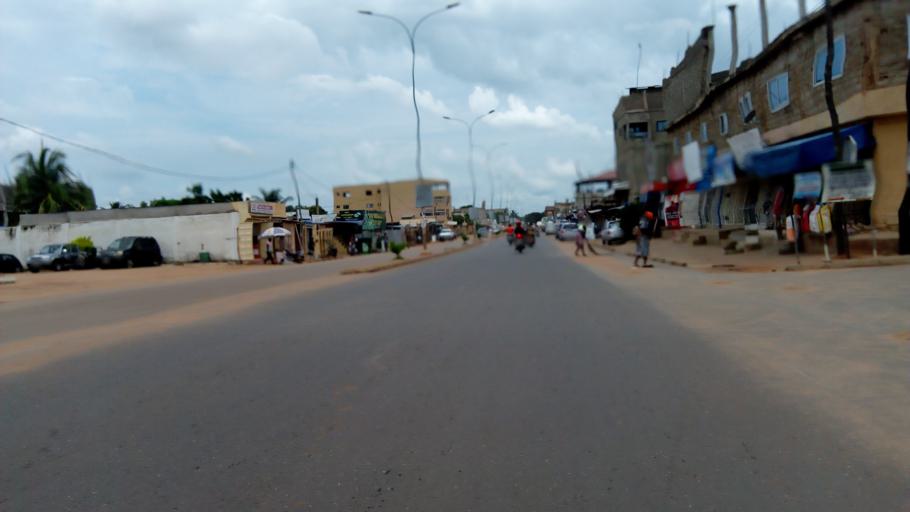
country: TG
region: Maritime
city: Lome
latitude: 6.2164
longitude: 1.1716
